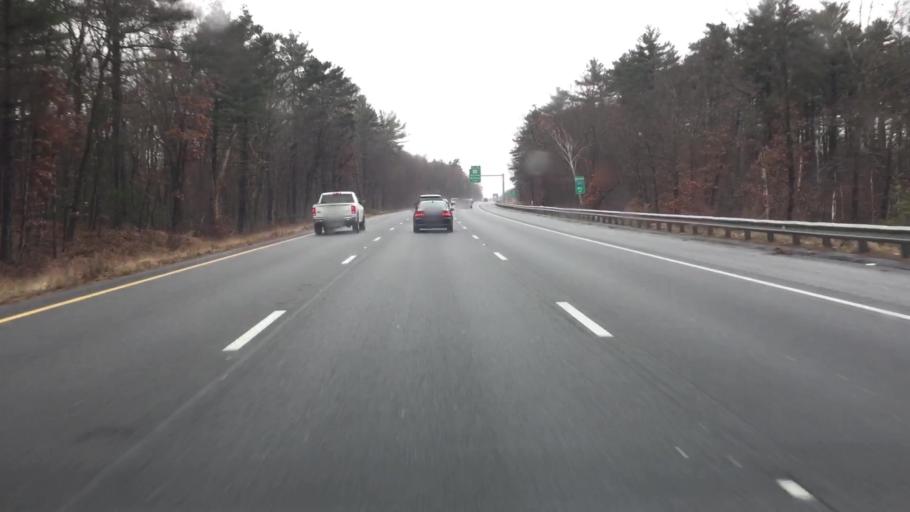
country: US
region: Massachusetts
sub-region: Norfolk County
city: Bellingham
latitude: 42.1290
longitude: -71.4748
